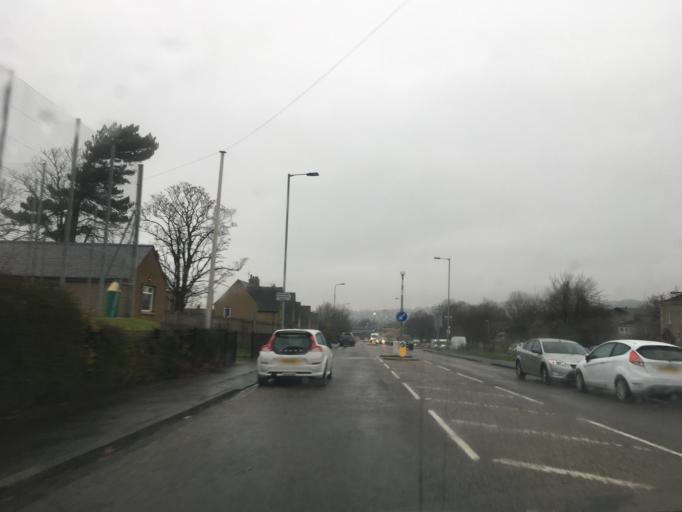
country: GB
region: Scotland
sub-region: Edinburgh
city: Colinton
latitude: 55.9291
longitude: -3.2723
